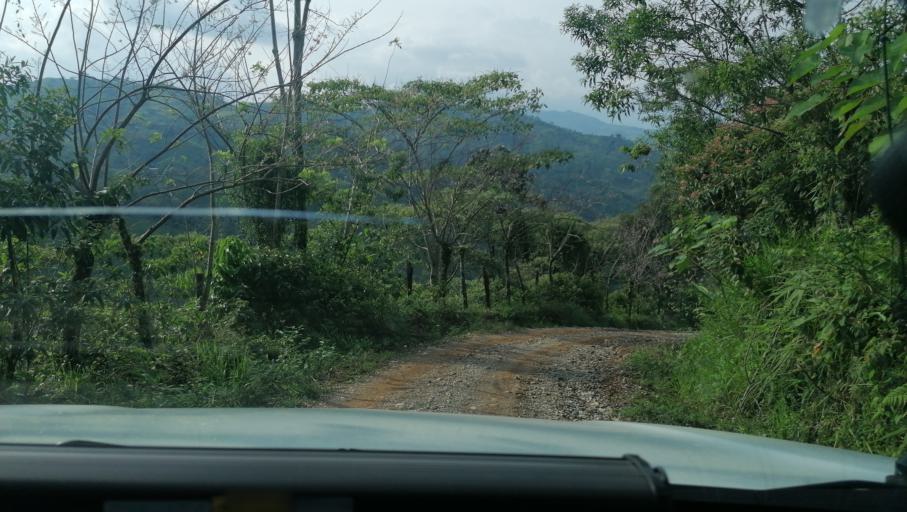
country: MX
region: Chiapas
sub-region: Tapilula
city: San Francisco Jacona
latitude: 17.3201
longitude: -93.0993
